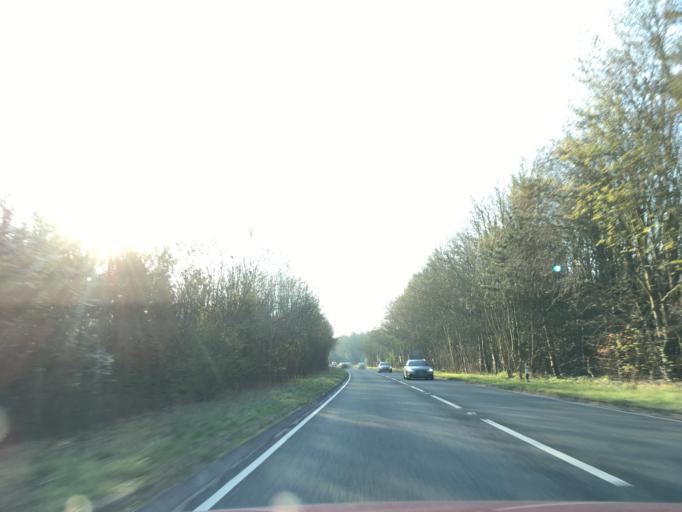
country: GB
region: England
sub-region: Gloucestershire
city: Northleach
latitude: 51.8276
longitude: -1.8093
